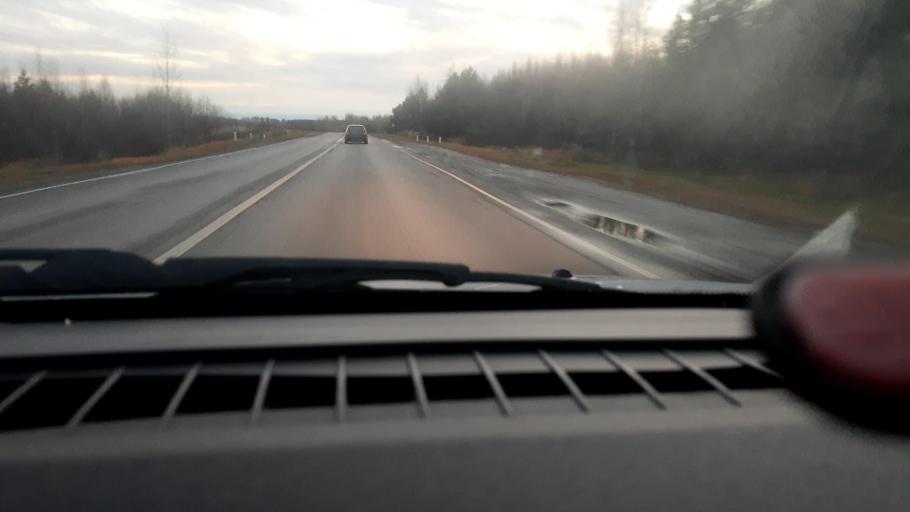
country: RU
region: Nizjnij Novgorod
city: Vladimirskoye
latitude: 56.9658
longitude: 45.1092
